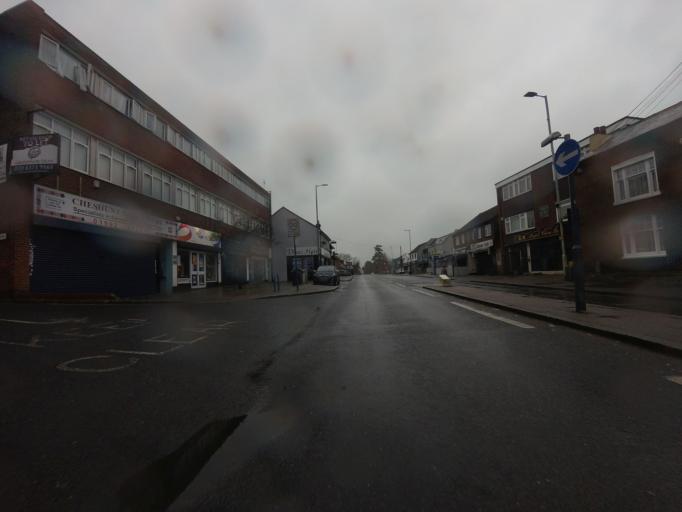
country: GB
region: England
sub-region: Hertfordshire
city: Cheshunt
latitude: 51.7028
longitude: -0.0345
